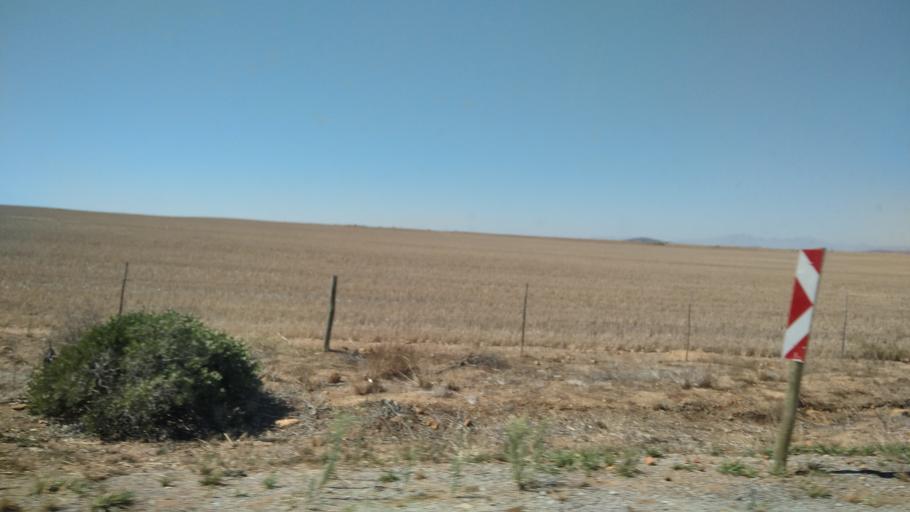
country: ZA
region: Western Cape
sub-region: West Coast District Municipality
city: Moorreesburg
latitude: -33.2238
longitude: 18.5486
